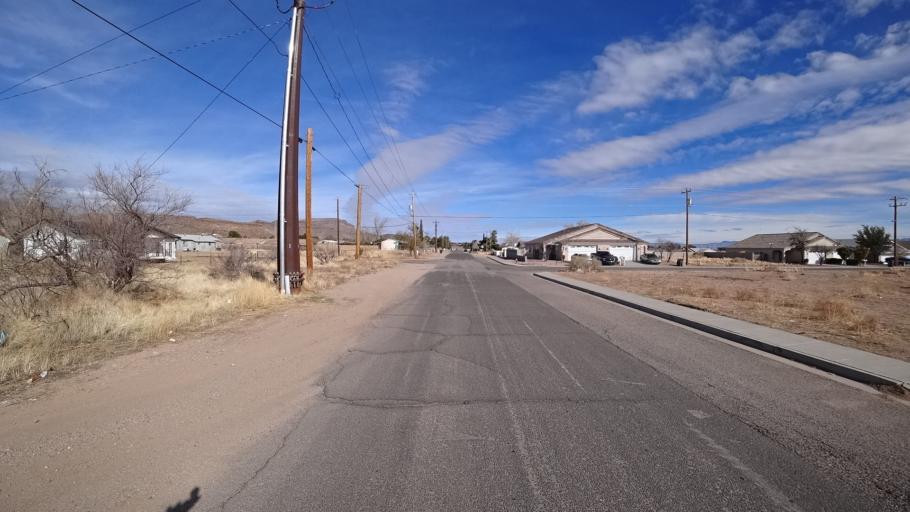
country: US
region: Arizona
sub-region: Mohave County
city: Kingman
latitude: 35.2174
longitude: -114.0446
